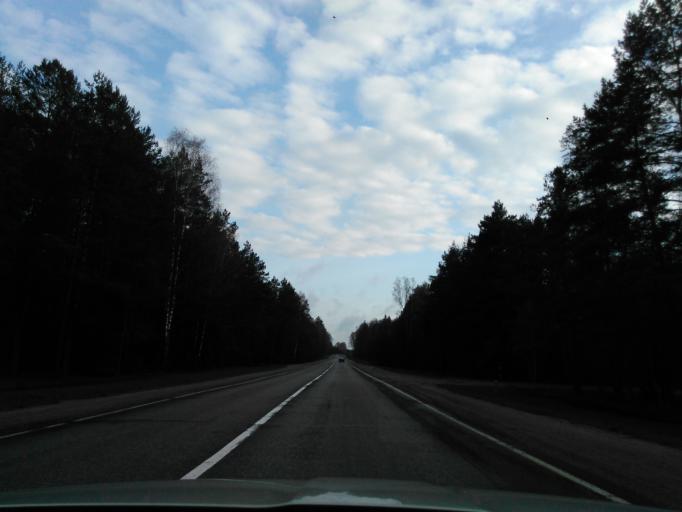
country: BY
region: Minsk
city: Lahoysk
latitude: 54.3001
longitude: 27.8746
